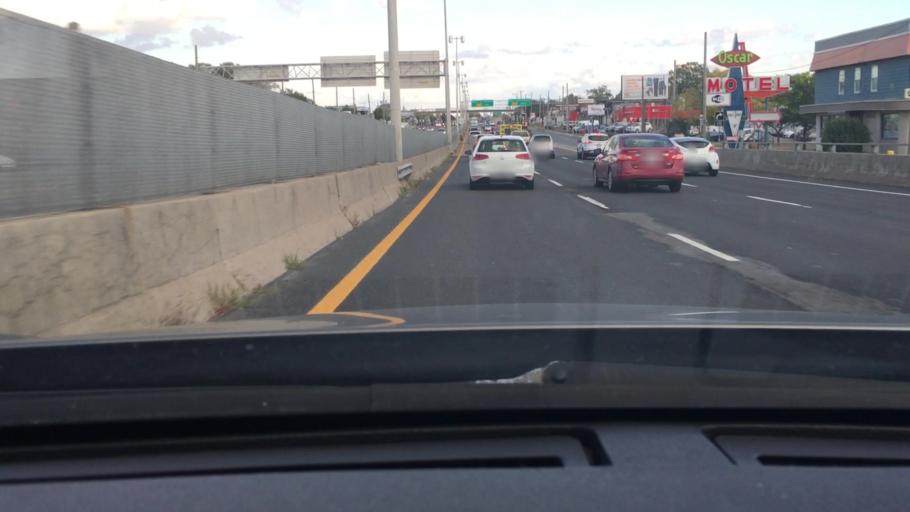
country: CA
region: Quebec
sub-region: Monteregie
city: Longueuil
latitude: 45.5134
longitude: -73.5027
